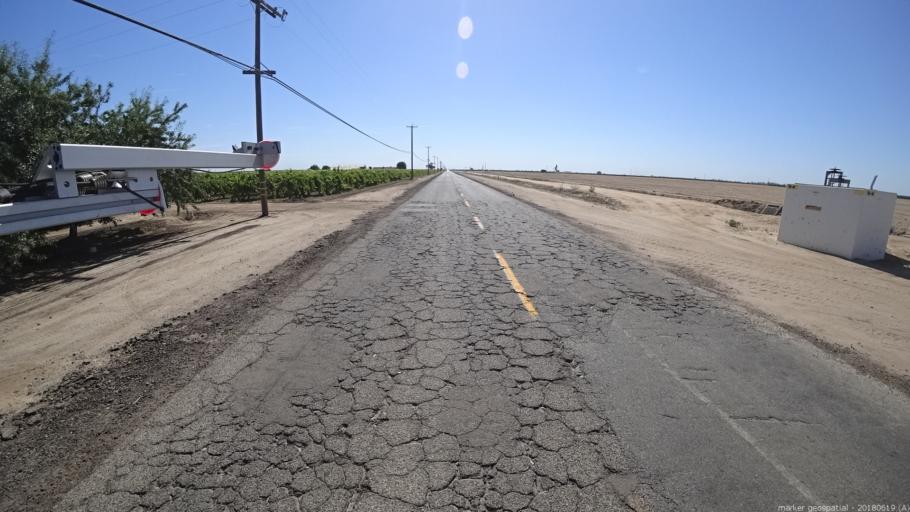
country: US
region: California
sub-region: Fresno County
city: Biola
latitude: 36.8367
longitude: -120.1420
